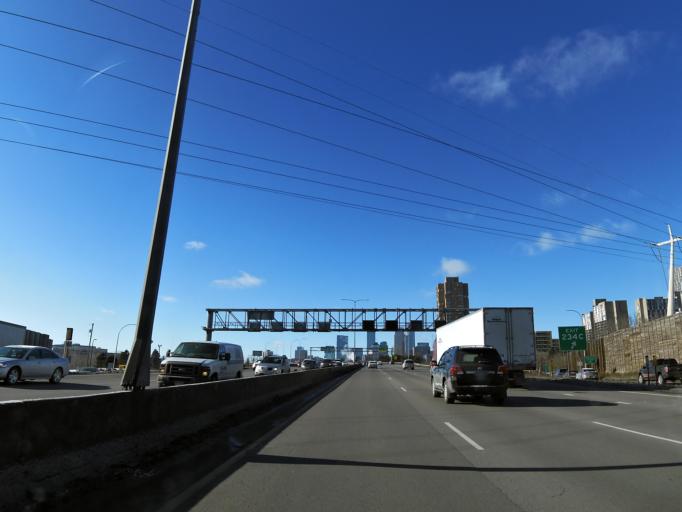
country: US
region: Minnesota
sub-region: Hennepin County
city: Minneapolis
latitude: 44.9651
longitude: -93.2454
